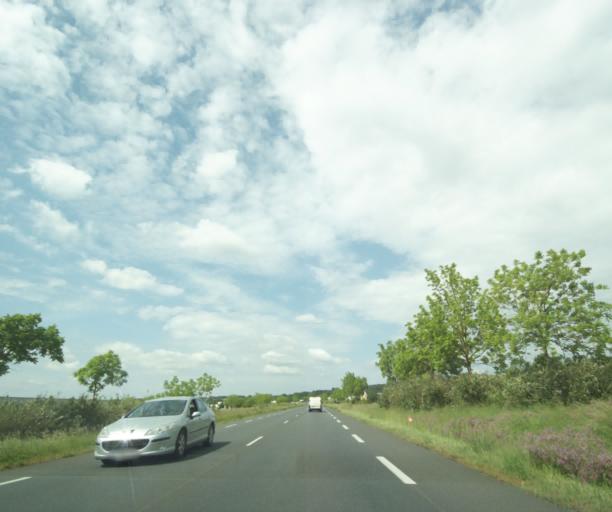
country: FR
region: Pays de la Loire
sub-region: Departement de Maine-et-Loire
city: Distre
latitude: 47.2295
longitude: -0.1140
